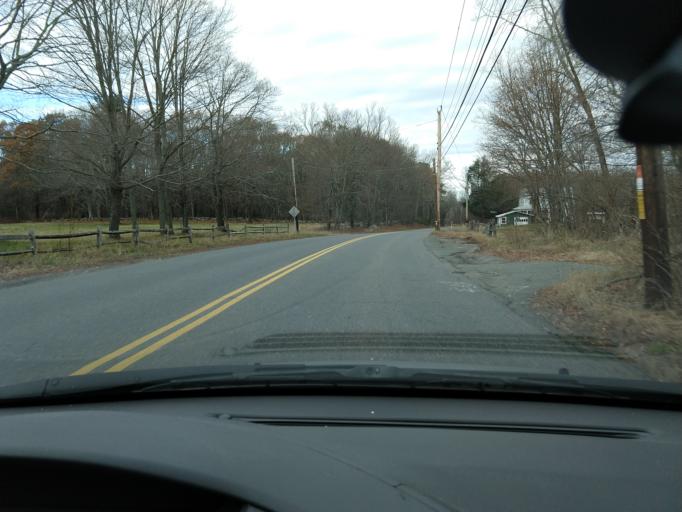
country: US
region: Massachusetts
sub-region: Middlesex County
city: Lincoln
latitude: 42.4535
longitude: -71.3106
